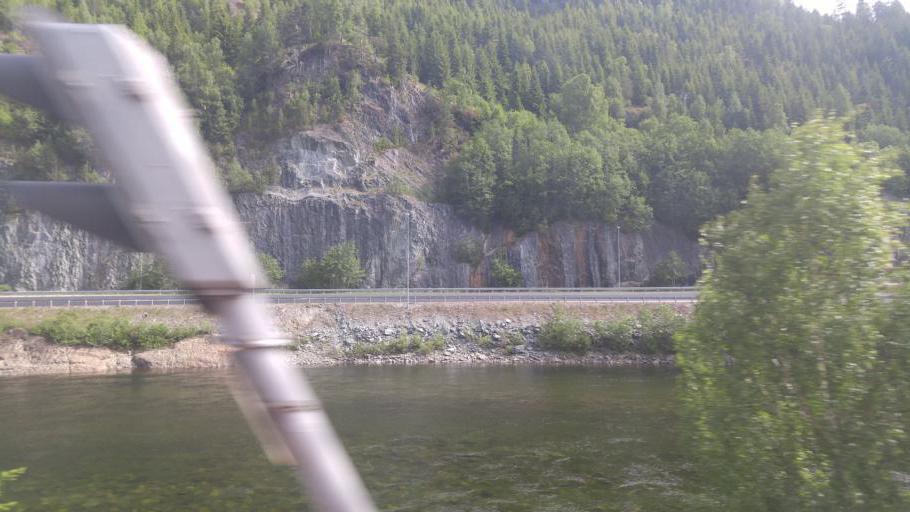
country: NO
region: Sor-Trondelag
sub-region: Midtre Gauldal
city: Storen
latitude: 63.0673
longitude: 10.2837
